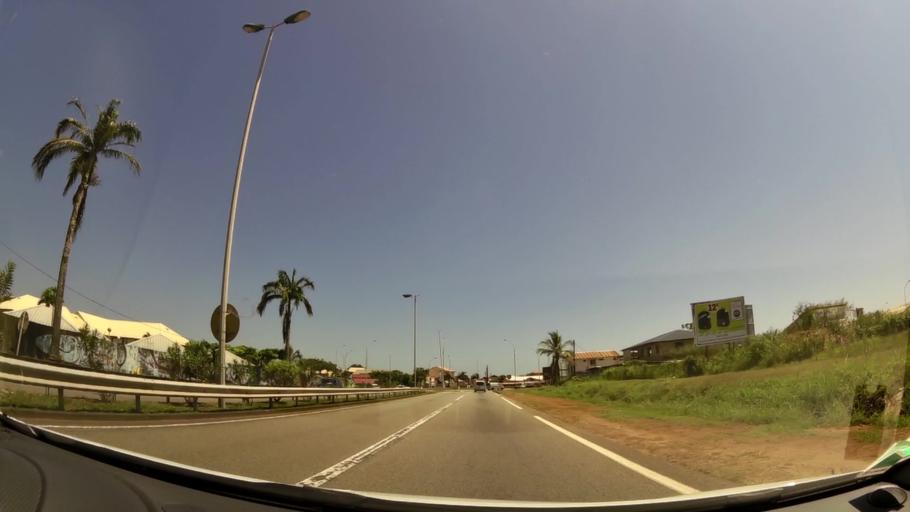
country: GF
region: Guyane
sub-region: Guyane
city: Cayenne
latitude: 4.9304
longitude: -52.3295
